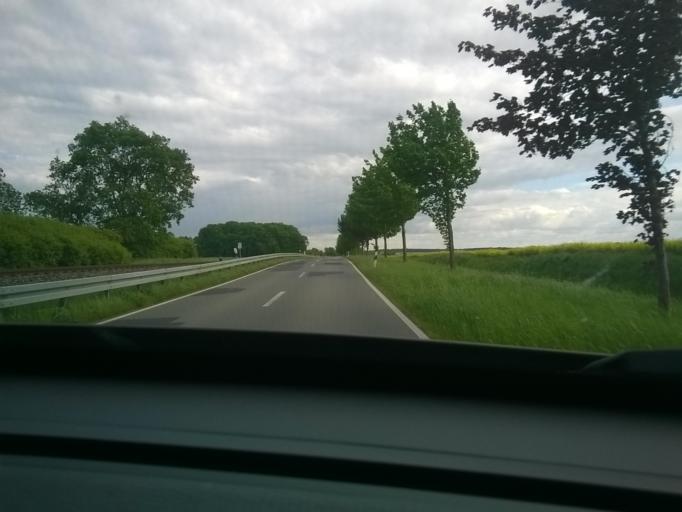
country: DE
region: Brandenburg
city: Wittstock
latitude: 53.1288
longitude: 12.5105
